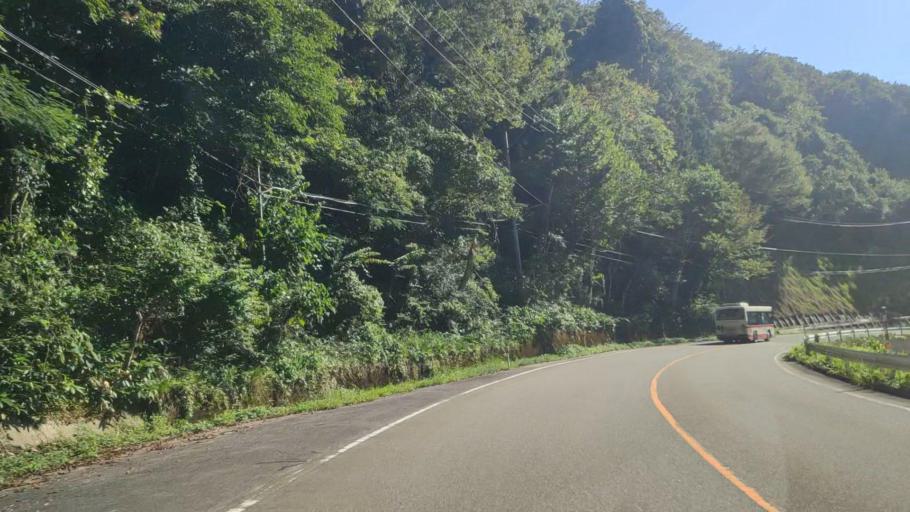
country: JP
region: Ishikawa
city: Nanao
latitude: 37.2376
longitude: 136.9796
